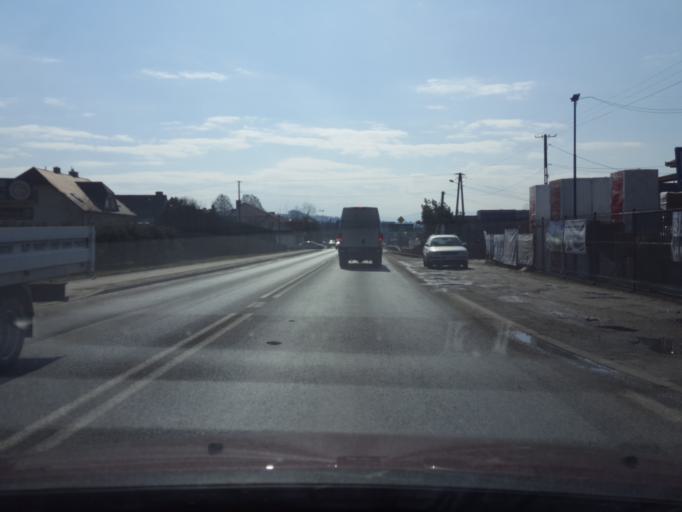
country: PL
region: Lesser Poland Voivodeship
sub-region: Powiat nowosadecki
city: Chelmiec
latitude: 49.6736
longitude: 20.6841
